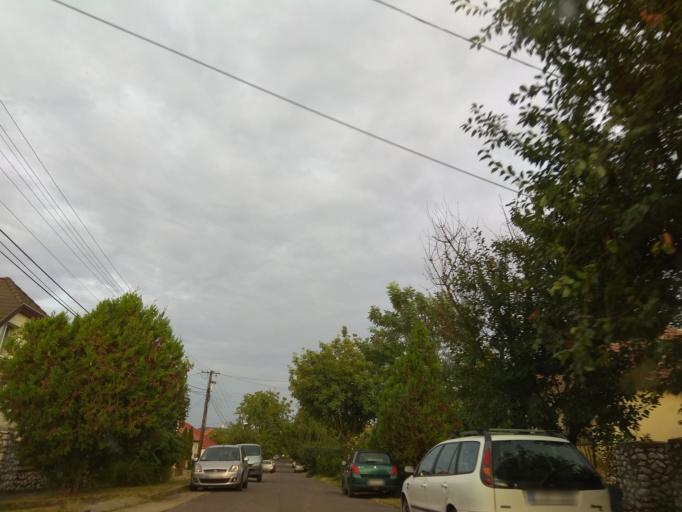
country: HU
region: Borsod-Abauj-Zemplen
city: Miskolc
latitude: 48.0519
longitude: 20.7898
